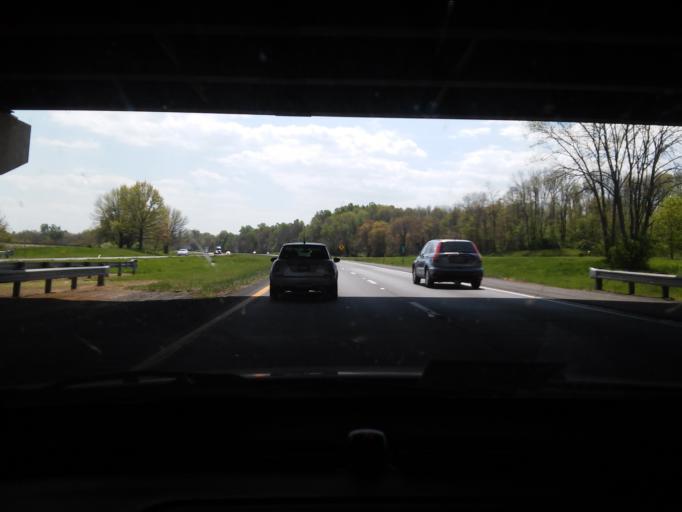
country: US
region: West Virginia
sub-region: Berkeley County
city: Inwood
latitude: 39.4068
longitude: -78.0243
